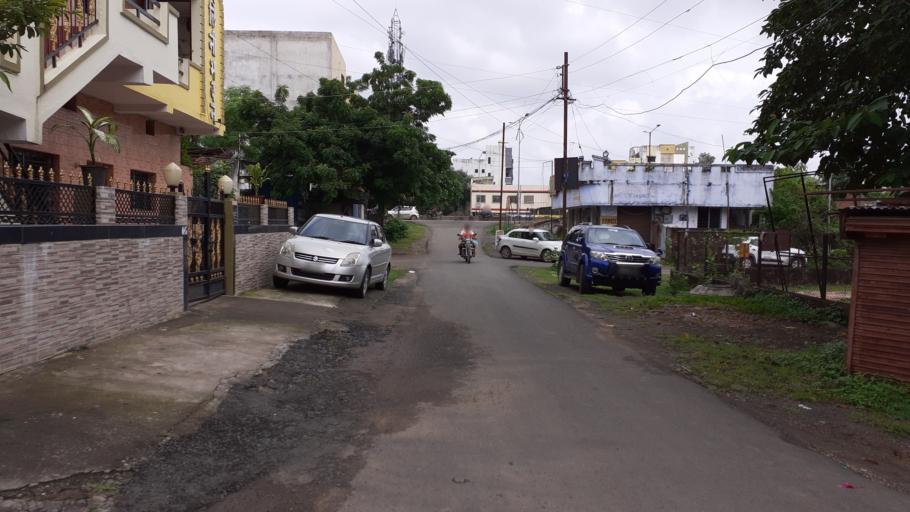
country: IN
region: Maharashtra
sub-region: Nagpur Division
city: Nagpur
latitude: 21.1056
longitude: 79.1145
